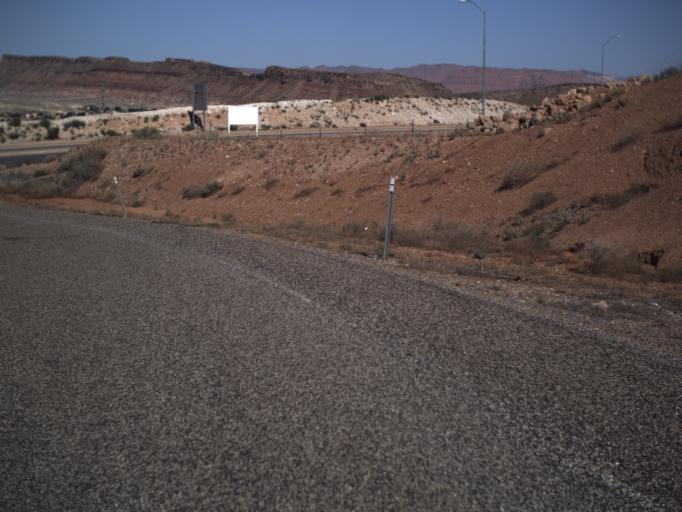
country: US
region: Utah
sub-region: Washington County
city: Saint George
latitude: 37.0258
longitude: -113.6003
